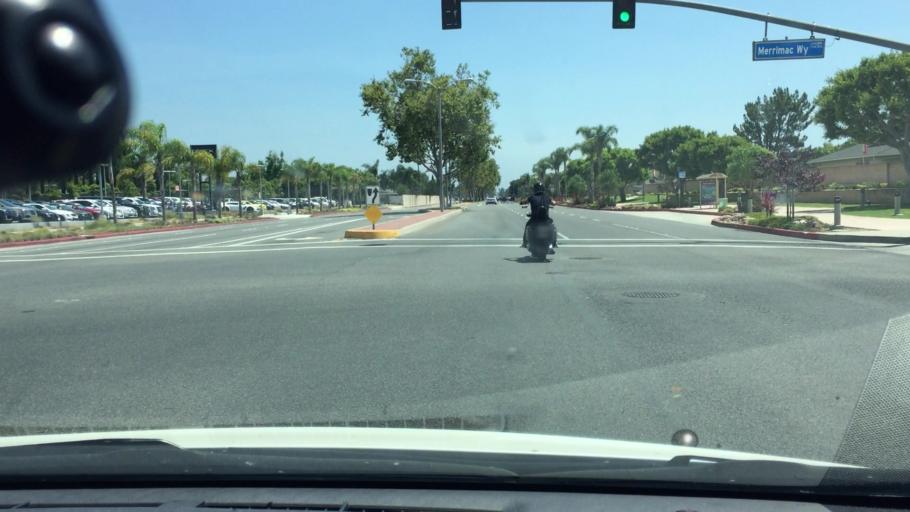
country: US
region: California
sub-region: Orange County
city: Costa Mesa
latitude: 33.6684
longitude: -117.9193
